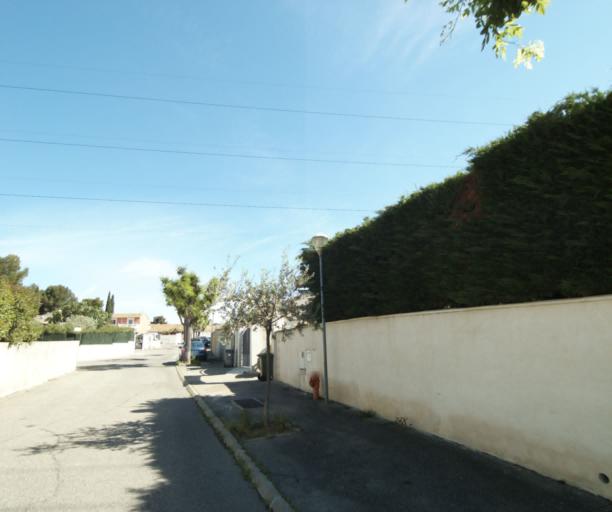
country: FR
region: Provence-Alpes-Cote d'Azur
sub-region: Departement des Bouches-du-Rhone
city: Rognac
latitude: 43.5073
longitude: 5.2205
